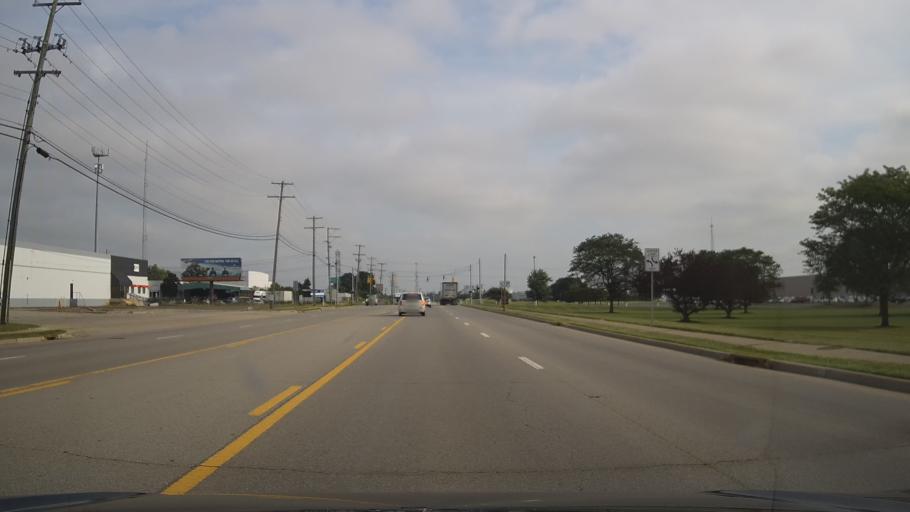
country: US
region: Ohio
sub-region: Franklin County
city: Lincoln Village
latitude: 39.9591
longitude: -83.1108
